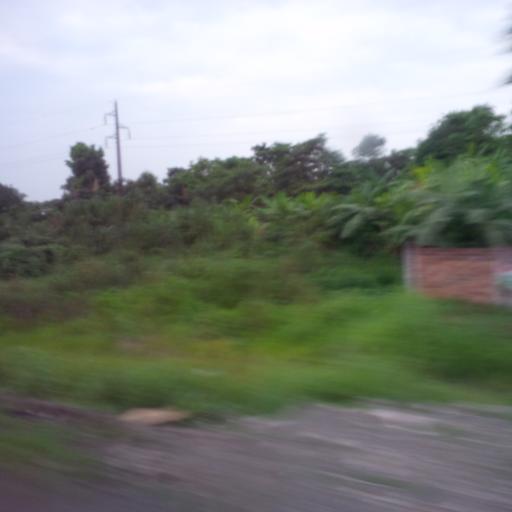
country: EC
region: Canar
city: La Troncal
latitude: -2.3401
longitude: -79.3836
